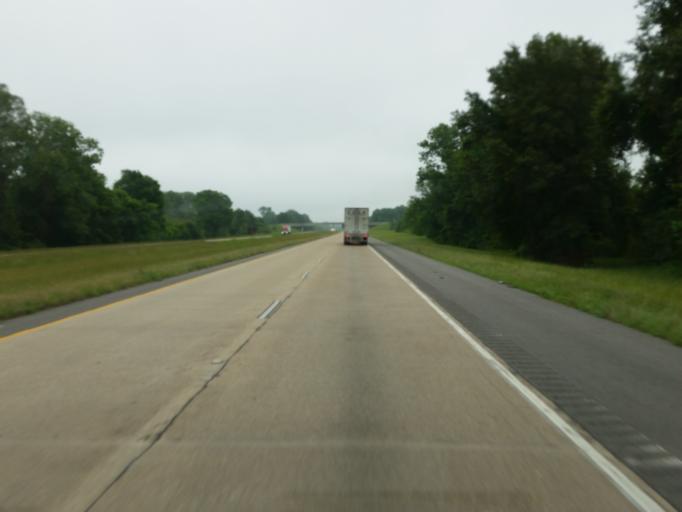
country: US
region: Louisiana
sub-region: Madison Parish
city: Tallulah
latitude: 32.3690
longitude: -91.1363
